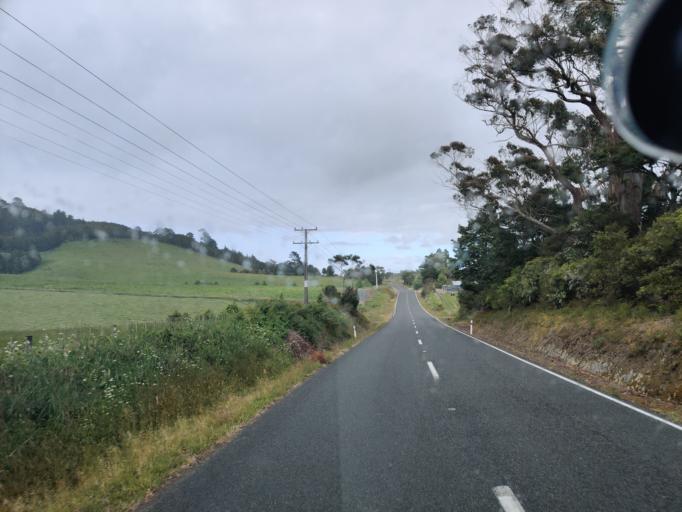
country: NZ
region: Northland
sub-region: Whangarei
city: Ngunguru
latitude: -35.5654
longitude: 174.3725
